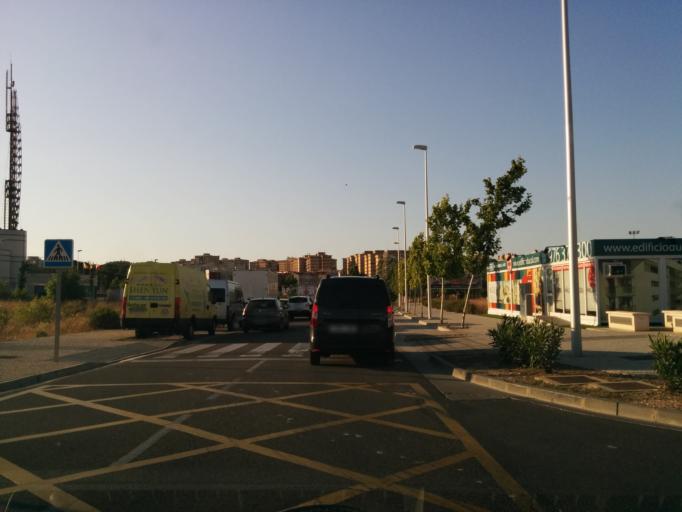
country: ES
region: Aragon
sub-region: Provincia de Zaragoza
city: Zaragoza
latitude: 41.6190
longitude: -0.8762
